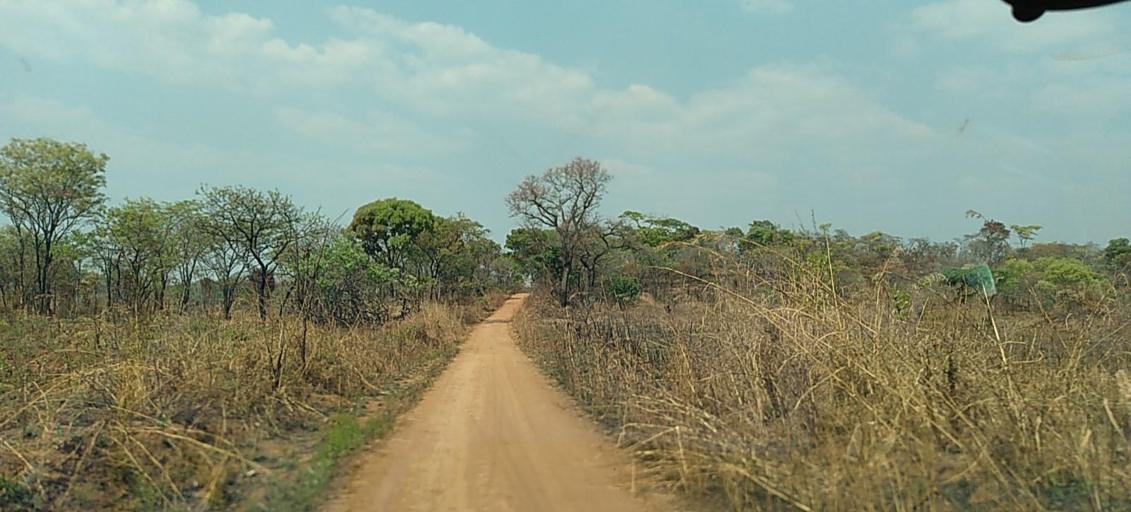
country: ZM
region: North-Western
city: Kasempa
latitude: -13.3070
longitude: 26.0693
